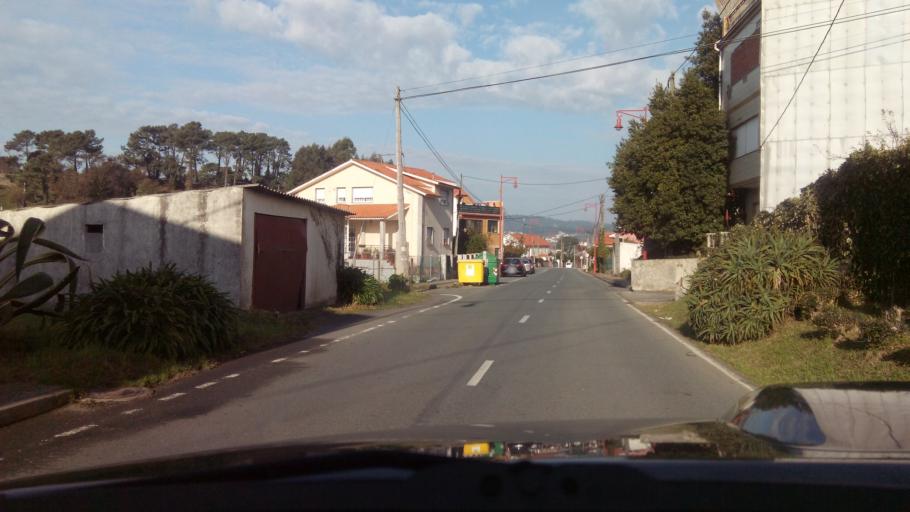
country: ES
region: Galicia
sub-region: Provincia de Pontevedra
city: Marin
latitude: 42.3688
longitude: -8.7346
